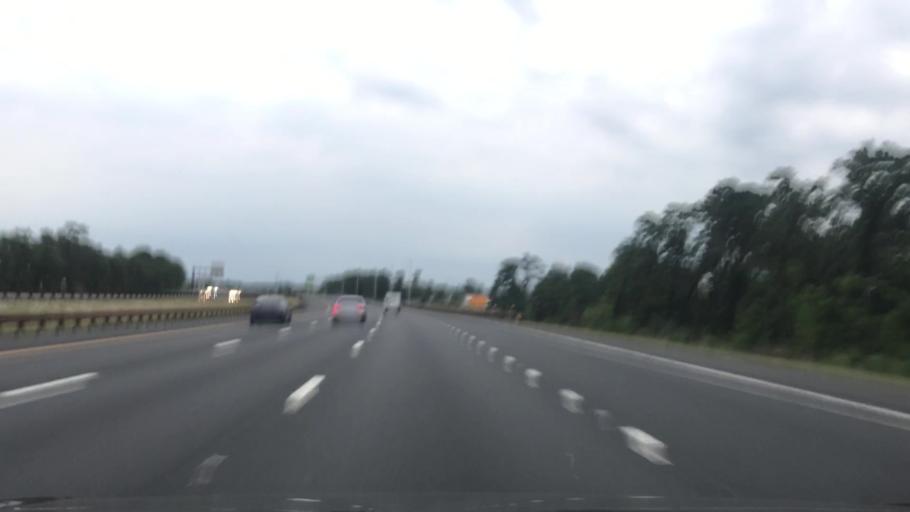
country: US
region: New Jersey
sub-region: Ocean County
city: Leisure Village
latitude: 40.0708
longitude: -74.1580
